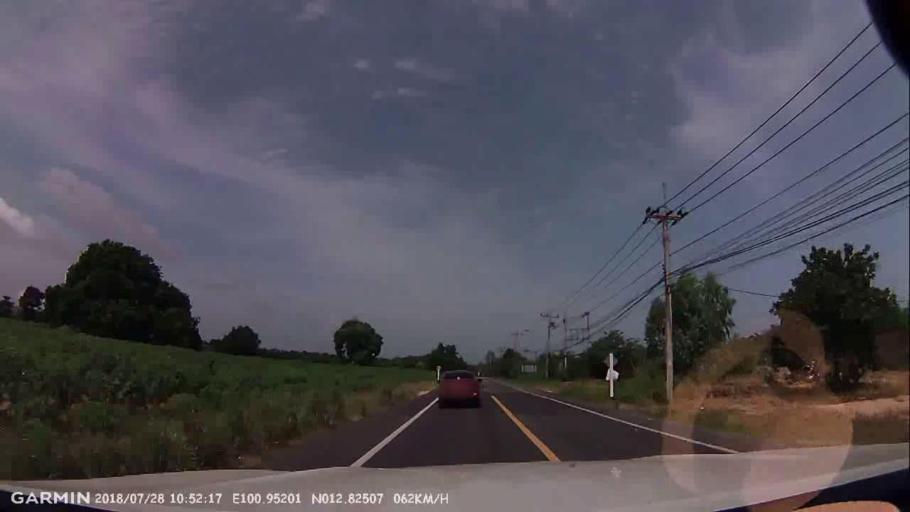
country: TH
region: Chon Buri
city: Phatthaya
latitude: 12.8250
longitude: 100.9519
